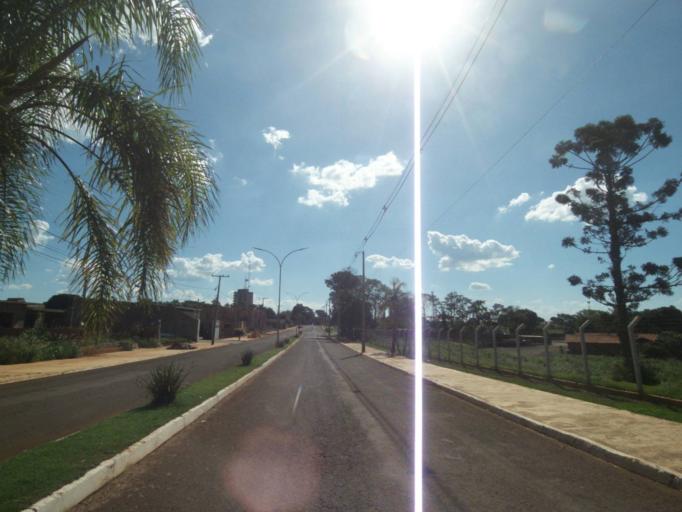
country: BR
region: Parana
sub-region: Sertanopolis
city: Sertanopolis
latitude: -23.0396
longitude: -50.8120
